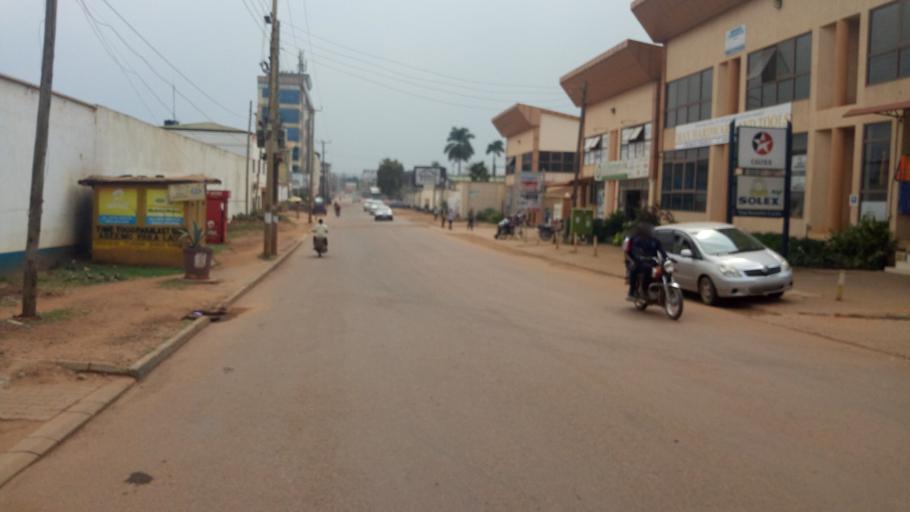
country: UG
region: Central Region
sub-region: Kampala District
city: Kampala
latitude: 0.3138
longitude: 32.6162
